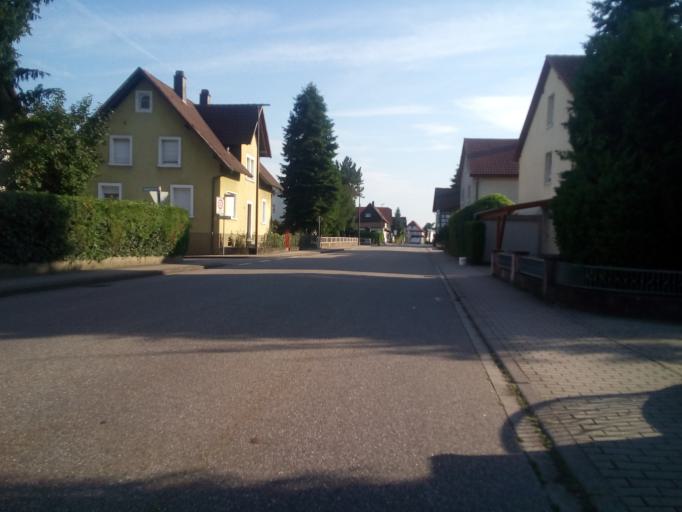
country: DE
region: Baden-Wuerttemberg
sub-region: Karlsruhe Region
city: Lichtenau
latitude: 48.7125
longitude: 7.9956
